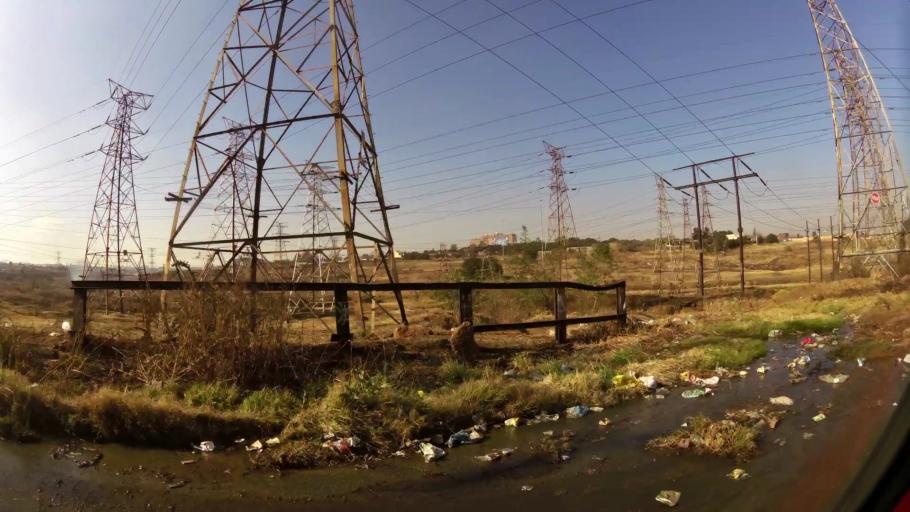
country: ZA
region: Gauteng
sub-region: City of Johannesburg Metropolitan Municipality
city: Soweto
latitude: -26.2530
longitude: 27.9320
